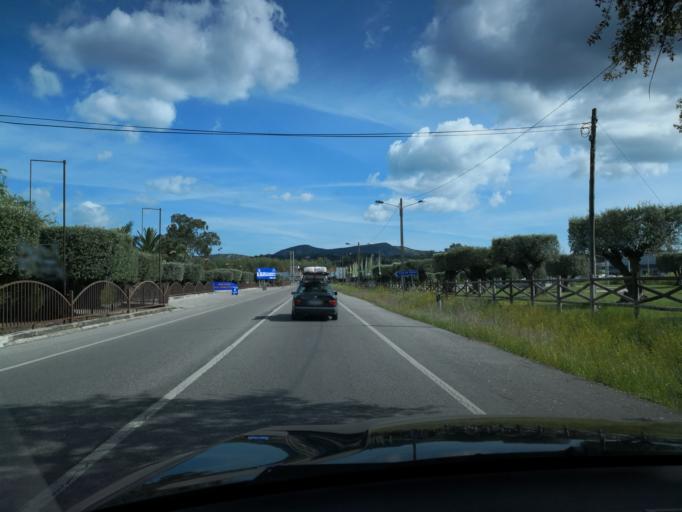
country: PT
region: Setubal
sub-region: Palmela
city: Quinta do Anjo
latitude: 38.5246
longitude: -9.0174
